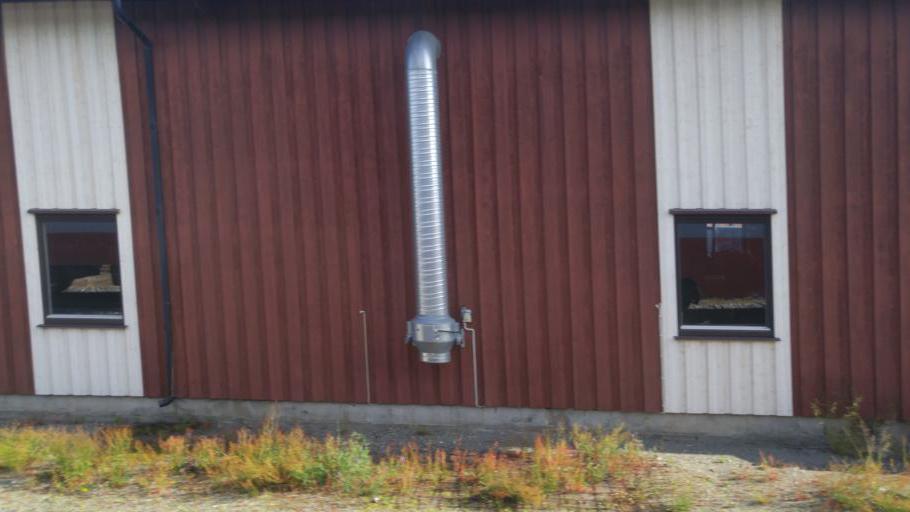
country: NO
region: Nord-Trondelag
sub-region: Stjordal
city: Stjordal
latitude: 63.4461
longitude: 10.9058
